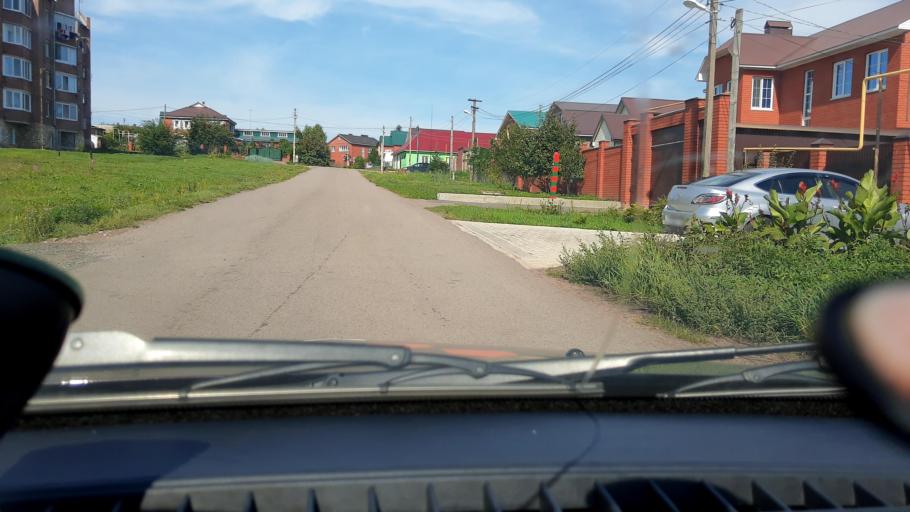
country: RU
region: Bashkortostan
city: Avdon
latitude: 54.6697
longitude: 55.7178
